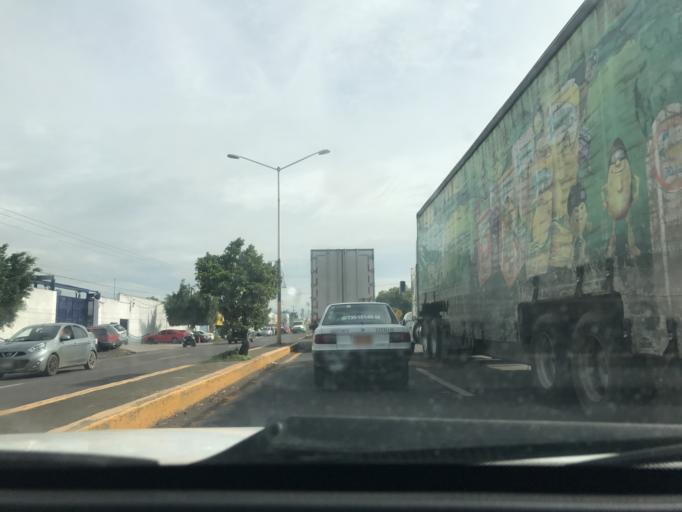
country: MX
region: Morelos
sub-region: Cuautla
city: Tierra Larga (Campo Nuevo)
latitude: 18.8635
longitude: -98.9314
